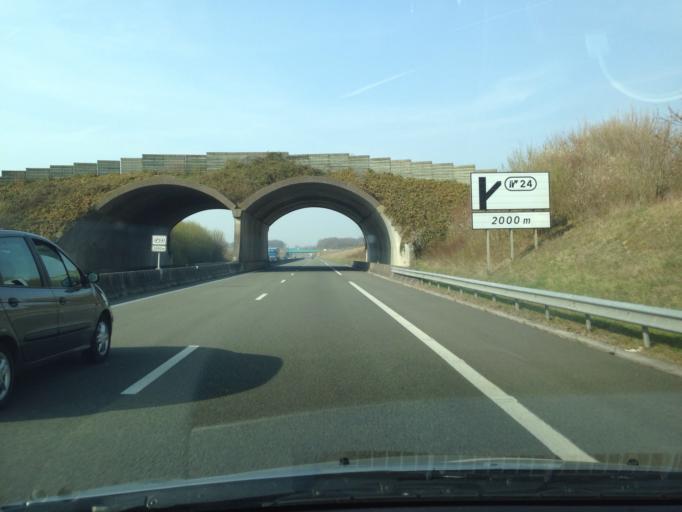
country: FR
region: Picardie
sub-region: Departement de la Somme
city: Nouvion
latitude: 50.2308
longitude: 1.7521
